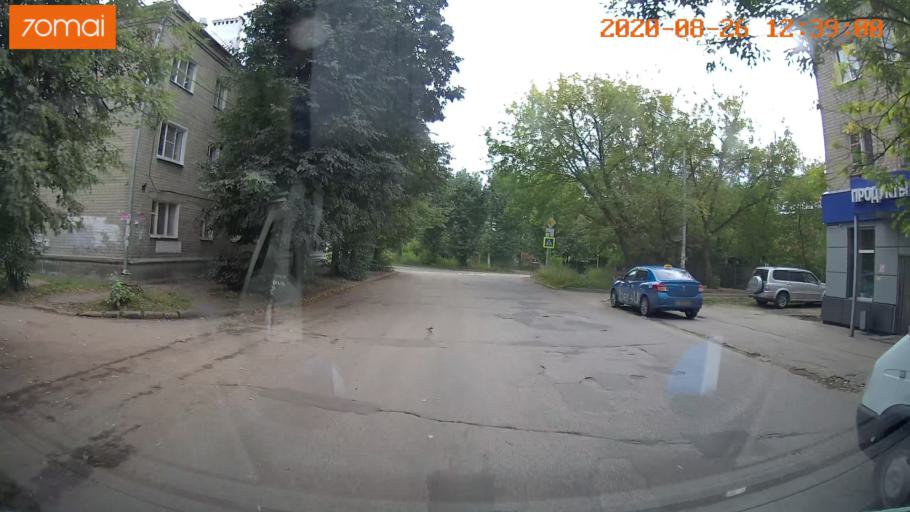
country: RU
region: Rjazan
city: Ryazan'
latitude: 54.6079
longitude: 39.7575
